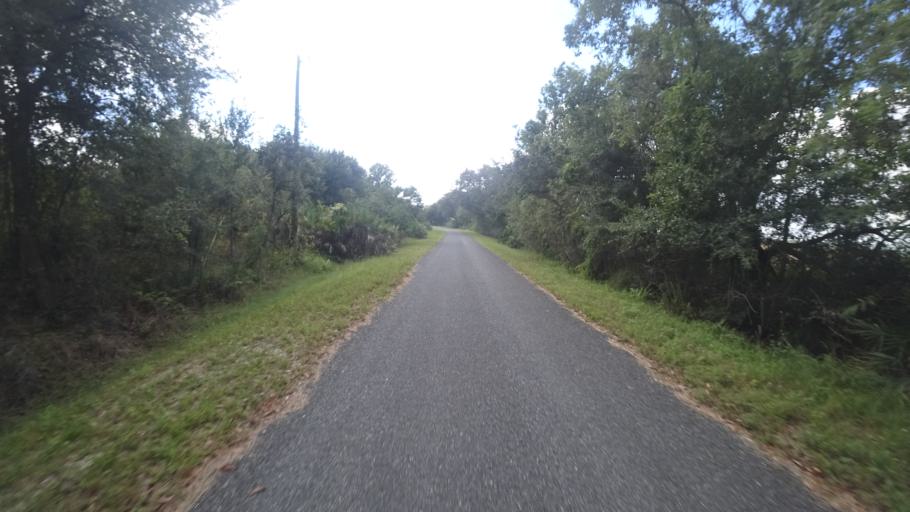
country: US
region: Florida
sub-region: Hillsborough County
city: Wimauma
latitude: 27.4752
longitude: -82.1706
